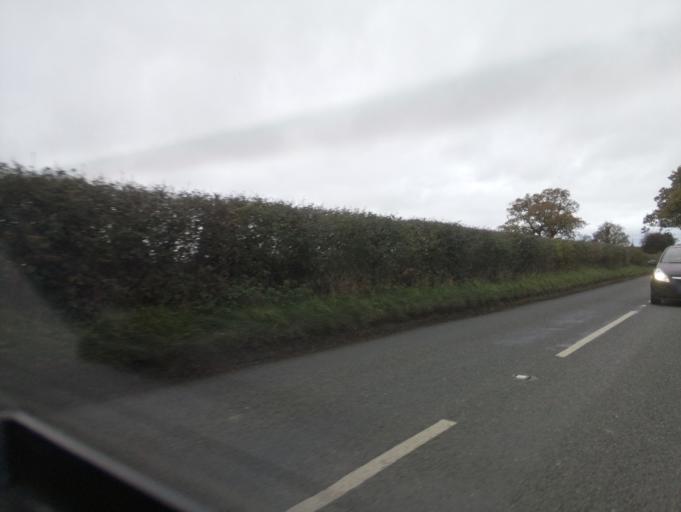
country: GB
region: England
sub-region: Dorset
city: Sherborne
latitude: 50.9771
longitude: -2.5615
